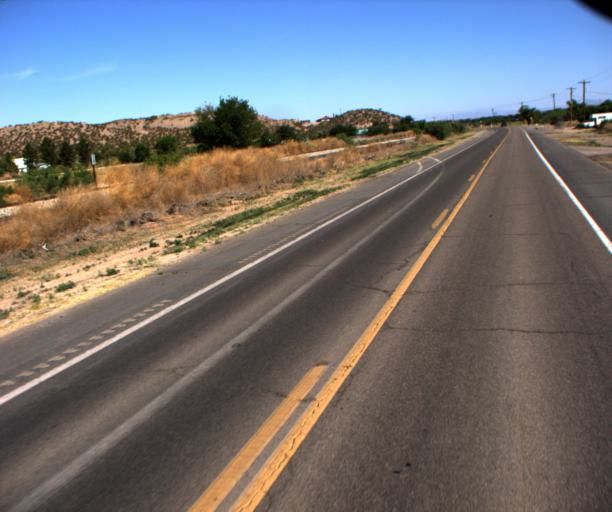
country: US
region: Arizona
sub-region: Greenlee County
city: Clifton
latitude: 32.7061
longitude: -109.0924
